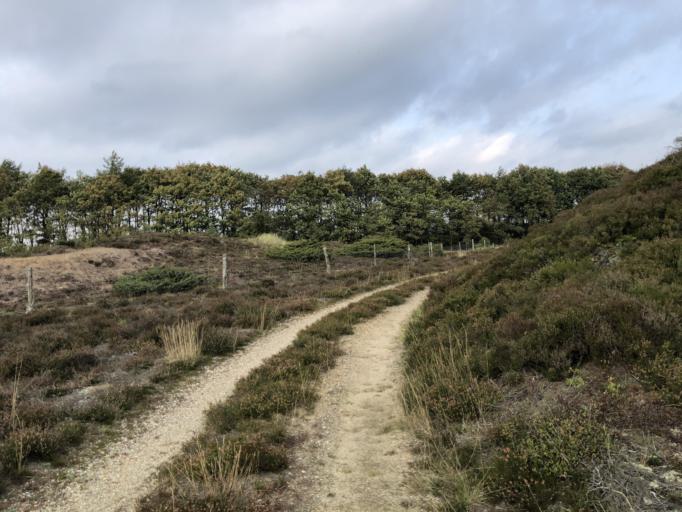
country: DK
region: Central Jutland
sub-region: Holstebro Kommune
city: Ulfborg
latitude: 56.2149
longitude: 8.4281
